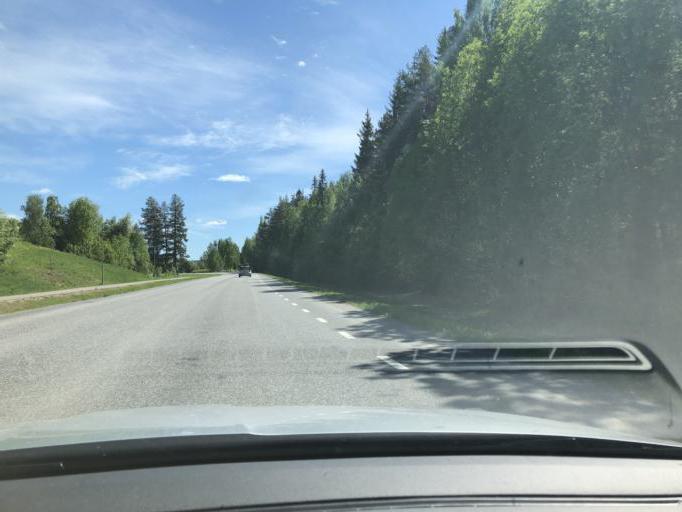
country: SE
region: Norrbotten
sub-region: Alvsbyns Kommun
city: AElvsbyn
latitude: 65.6672
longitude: 21.0258
